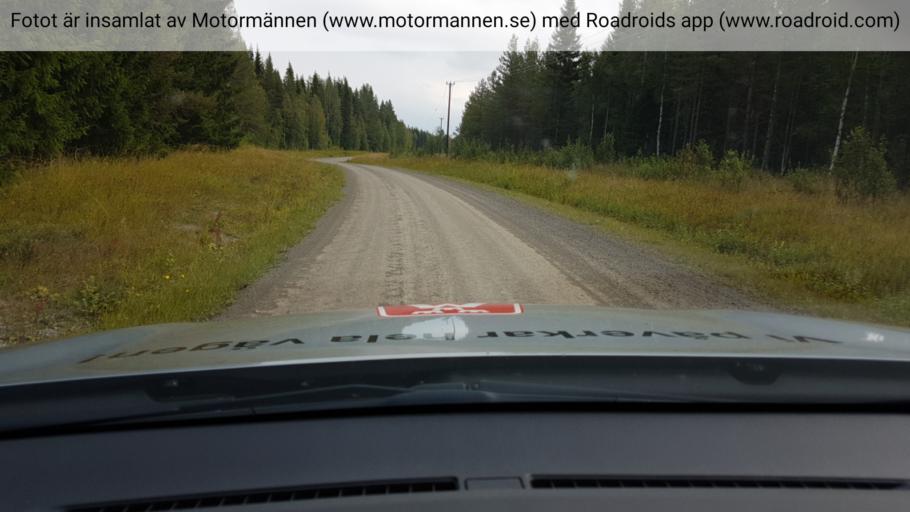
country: SE
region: Jaemtland
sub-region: Stroemsunds Kommun
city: Stroemsund
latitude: 63.7374
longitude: 15.4150
